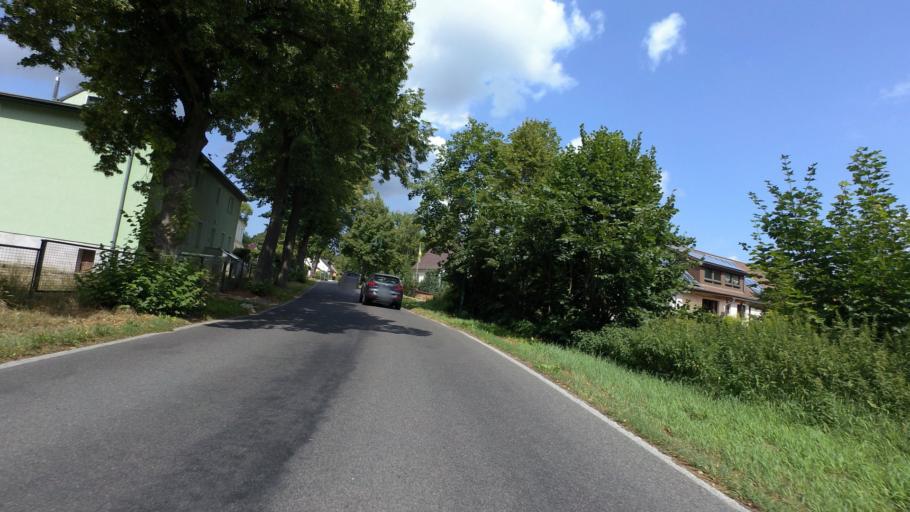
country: DE
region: Brandenburg
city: Teupitz
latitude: 52.1308
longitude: 13.5884
